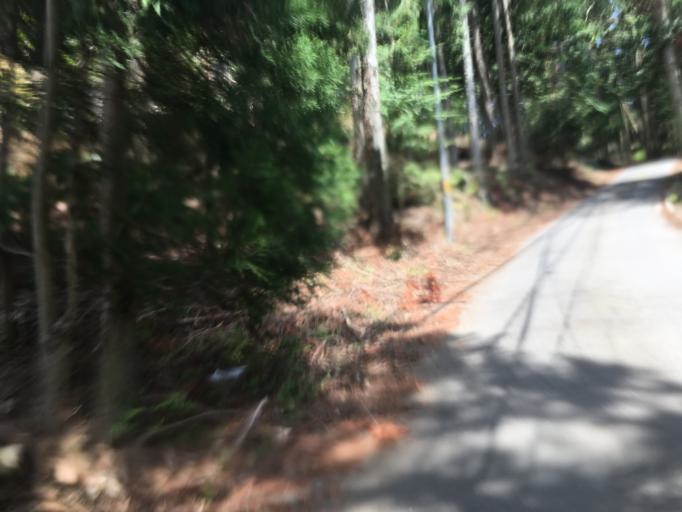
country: JP
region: Kyoto
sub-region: Kyoto-shi
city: Kamigyo-ku
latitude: 35.0744
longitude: 135.7175
